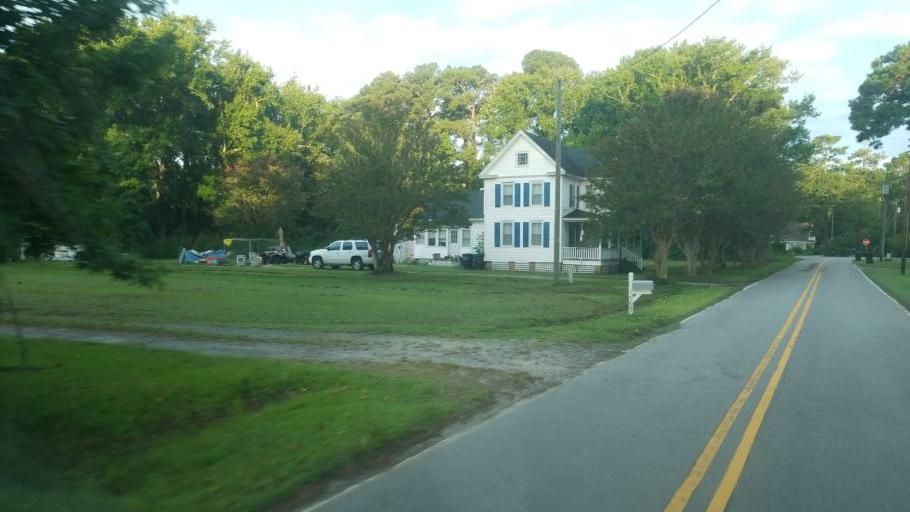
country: US
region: North Carolina
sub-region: Dare County
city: Wanchese
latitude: 35.8432
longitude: -75.6411
